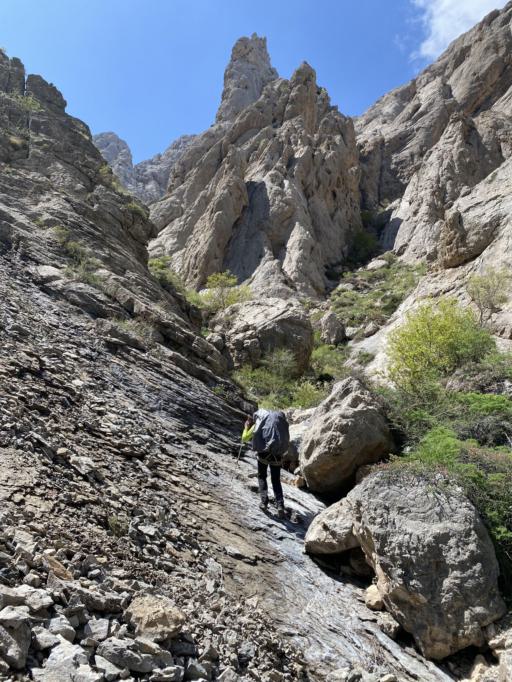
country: KZ
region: Ongtustik Qazaqstan
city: Ashchysay
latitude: 43.7673
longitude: 68.7936
